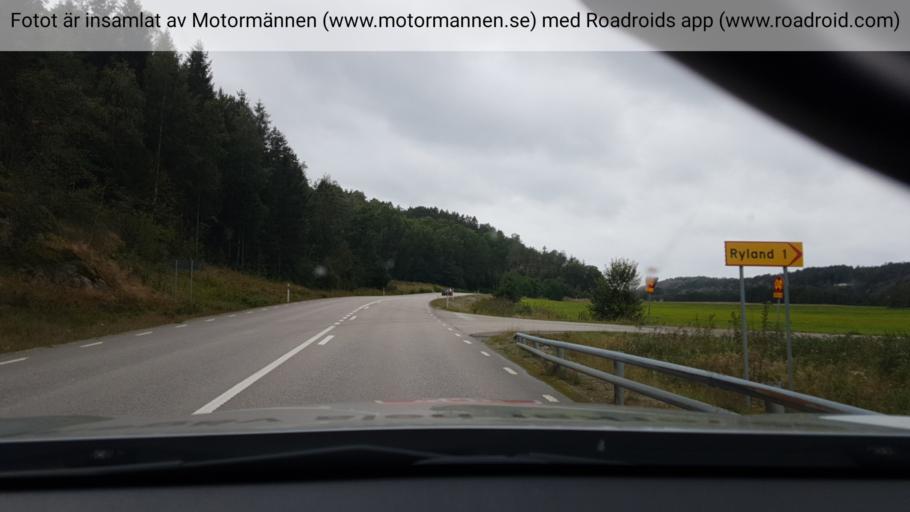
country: SE
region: Vaestra Goetaland
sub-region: Tanums Kommun
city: Tanumshede
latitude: 58.7327
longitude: 11.3173
